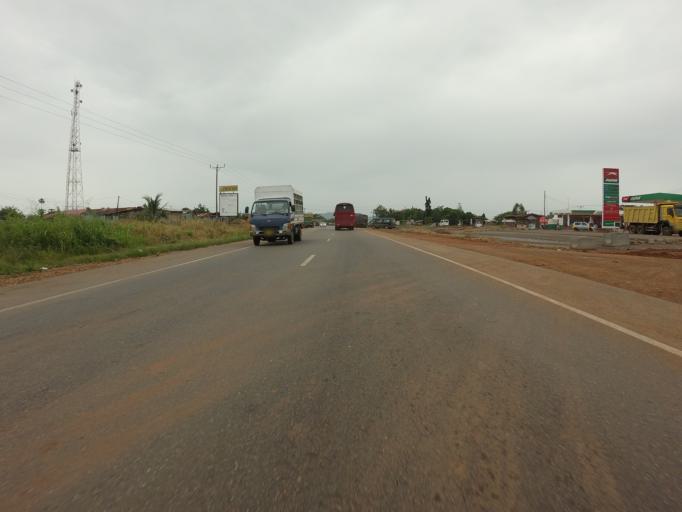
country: GH
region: Eastern
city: Suhum
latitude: 6.0517
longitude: -0.4623
